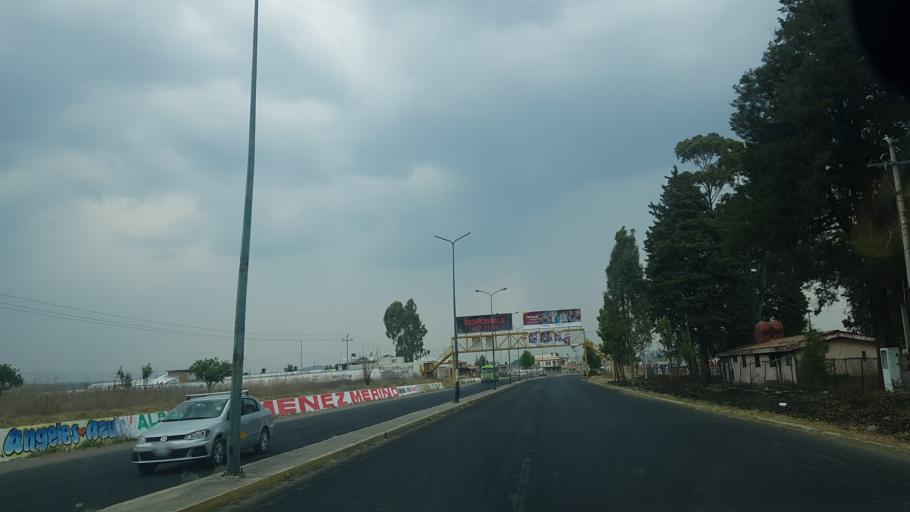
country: MX
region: Puebla
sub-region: Huejotzingo
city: Los Encinos
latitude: 19.1770
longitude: -98.4151
